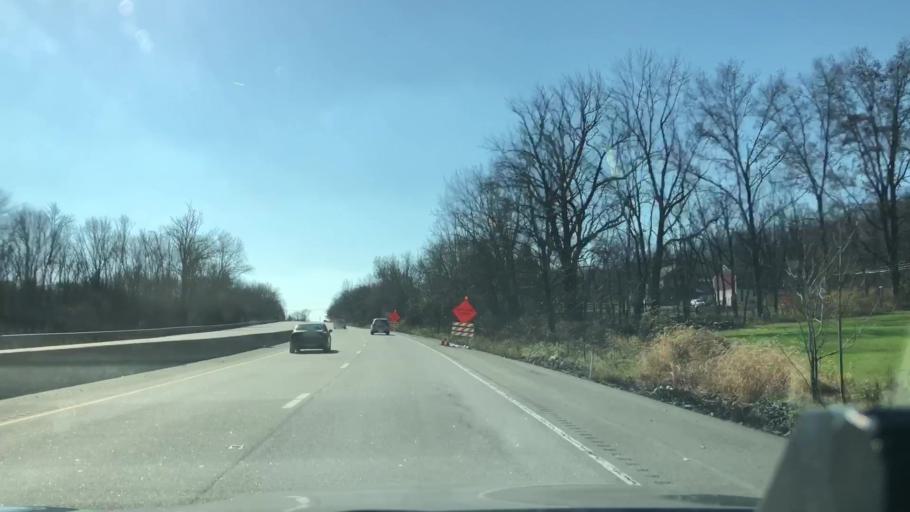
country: US
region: Pennsylvania
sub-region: Montgomery County
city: Halfway House
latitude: 40.2759
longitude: -75.6461
